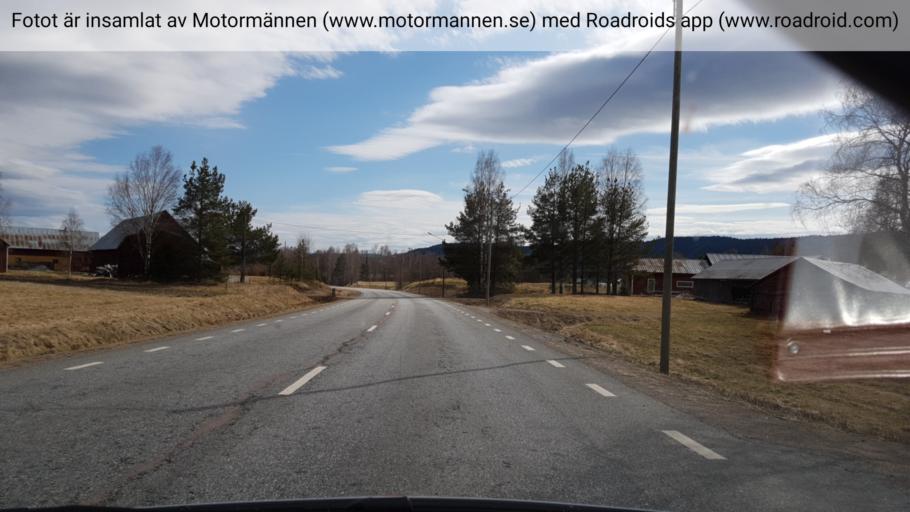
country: SE
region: Vaesternorrland
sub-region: Solleftea Kommun
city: Solleftea
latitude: 63.2459
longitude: 17.2087
